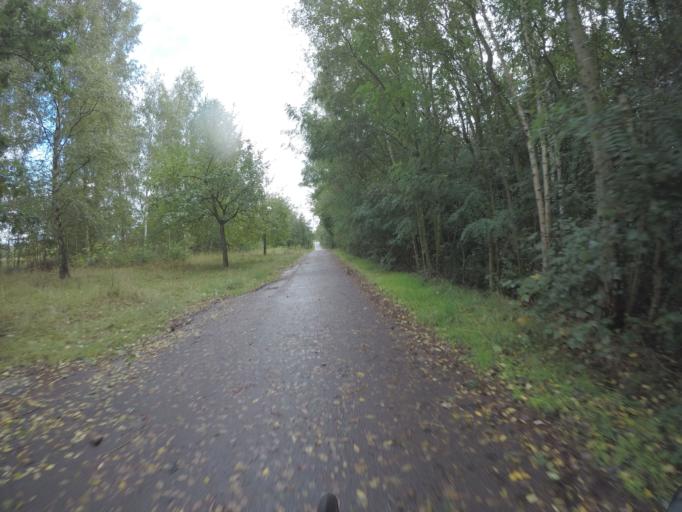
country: DE
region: Berlin
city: Blankenfelde
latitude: 52.6185
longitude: 13.3734
